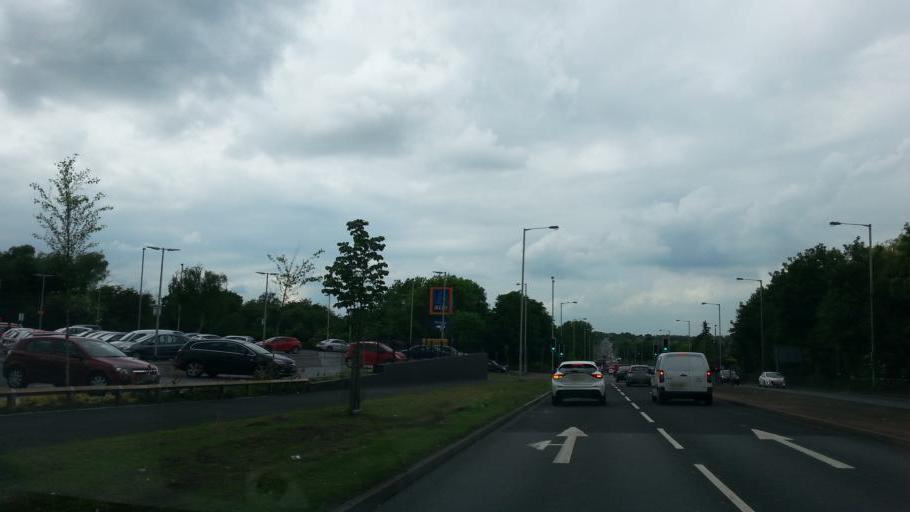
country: GB
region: England
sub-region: Sandwell
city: Tipton
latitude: 52.5268
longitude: -2.0847
